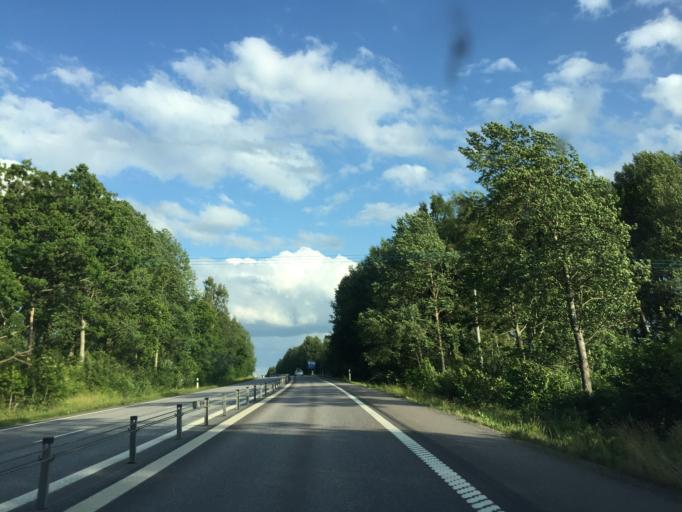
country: SE
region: OEstergoetland
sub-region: Motala Kommun
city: Motala
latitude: 58.5691
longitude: 14.9932
